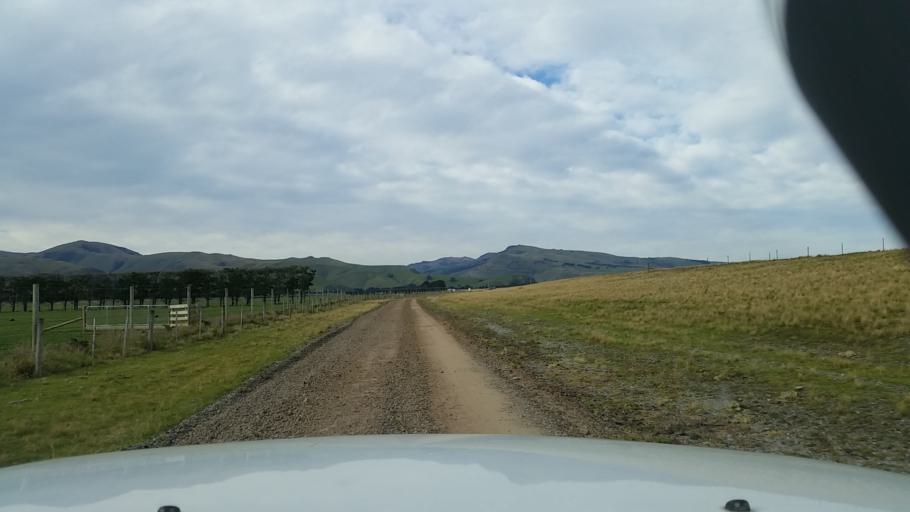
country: NZ
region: Canterbury
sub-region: Selwyn District
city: Lincoln
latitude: -43.8127
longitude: 172.6444
